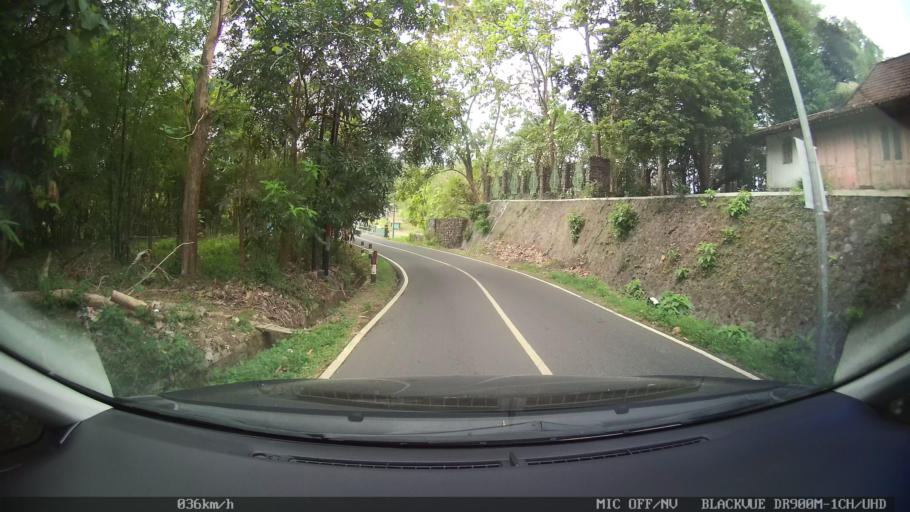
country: ID
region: Daerah Istimewa Yogyakarta
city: Depok
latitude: -7.8081
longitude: 110.4585
